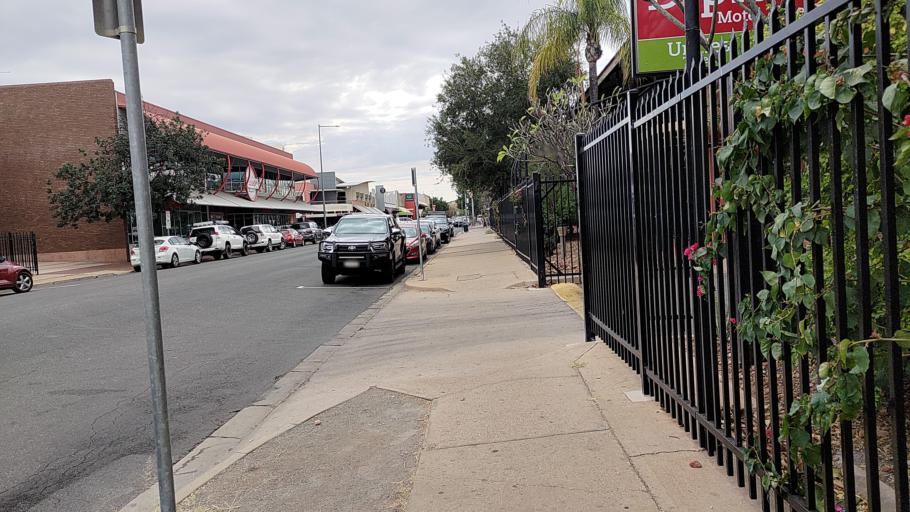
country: AU
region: Northern Territory
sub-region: Alice Springs
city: Alice Springs
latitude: -23.7011
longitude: 133.8806
